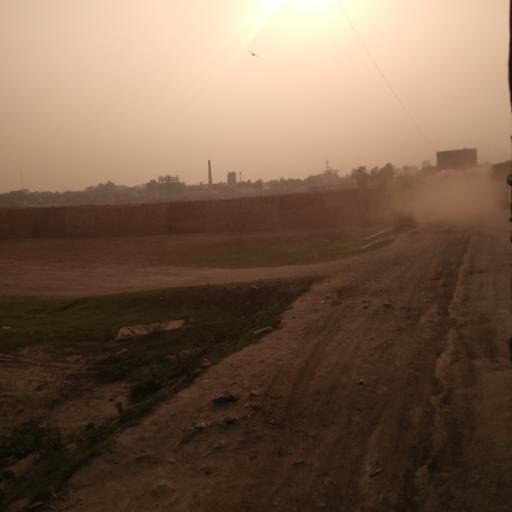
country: BD
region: Dhaka
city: Tungi
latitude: 23.8962
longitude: 90.3386
